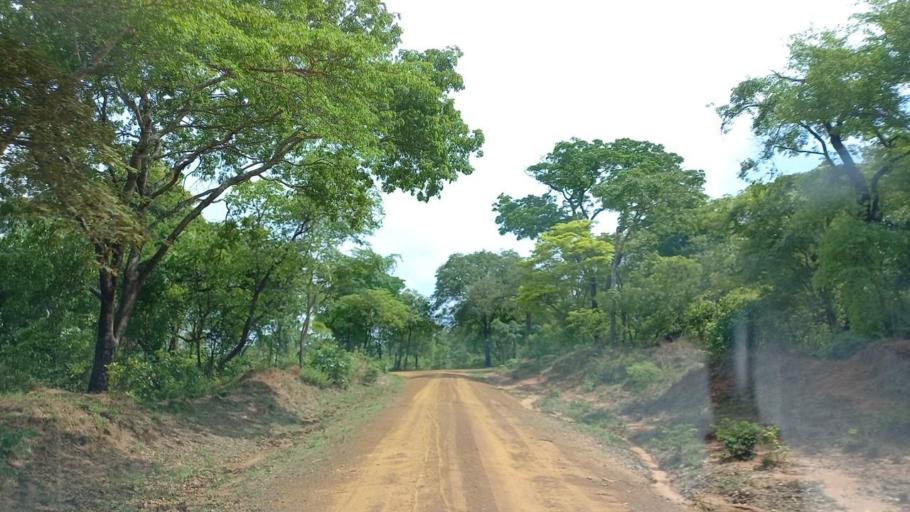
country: ZM
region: North-Western
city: Kabompo
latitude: -13.5429
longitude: 24.1000
